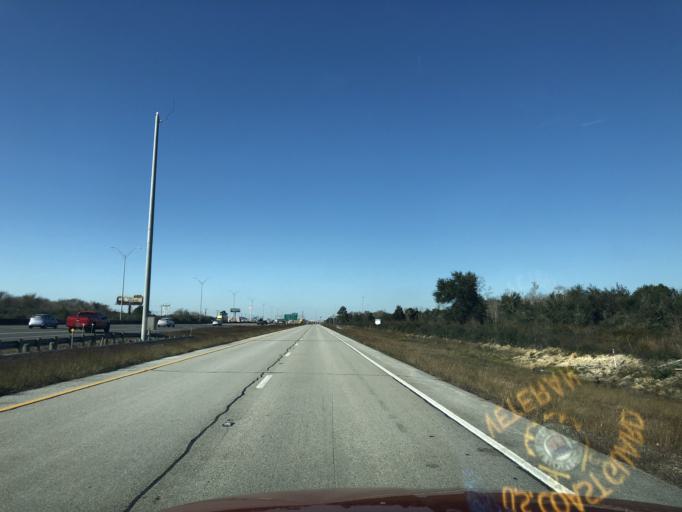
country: US
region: Texas
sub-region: Galveston County
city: Hitchcock
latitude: 29.3959
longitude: -95.0258
